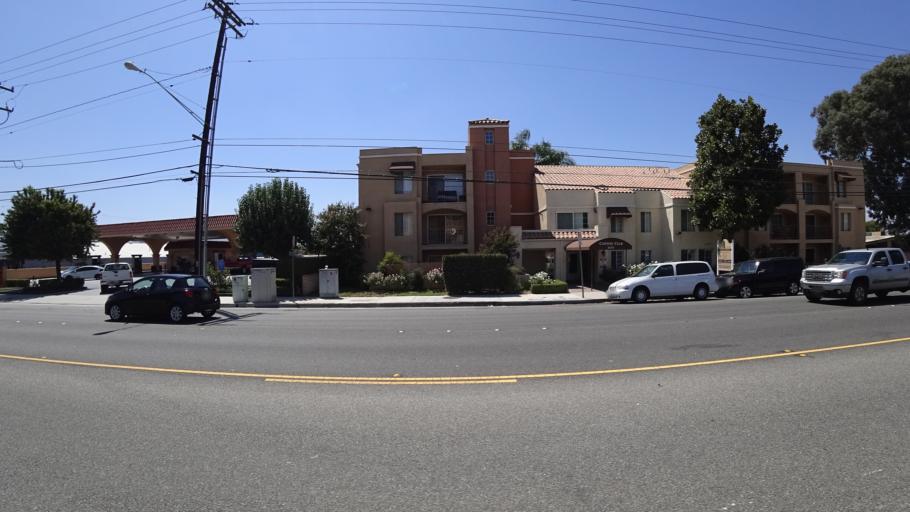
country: US
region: California
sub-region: Los Angeles County
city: Santa Clarita
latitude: 34.4157
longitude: -118.5414
